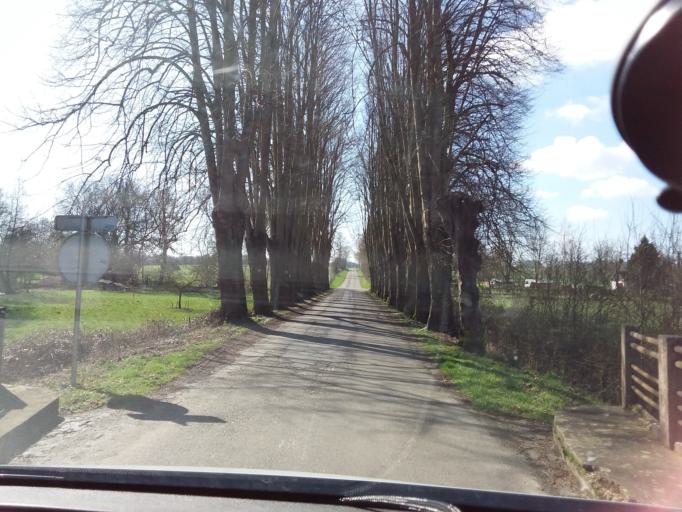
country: FR
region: Picardie
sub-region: Departement de l'Aisne
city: Hirson
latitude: 49.8756
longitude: 4.0920
